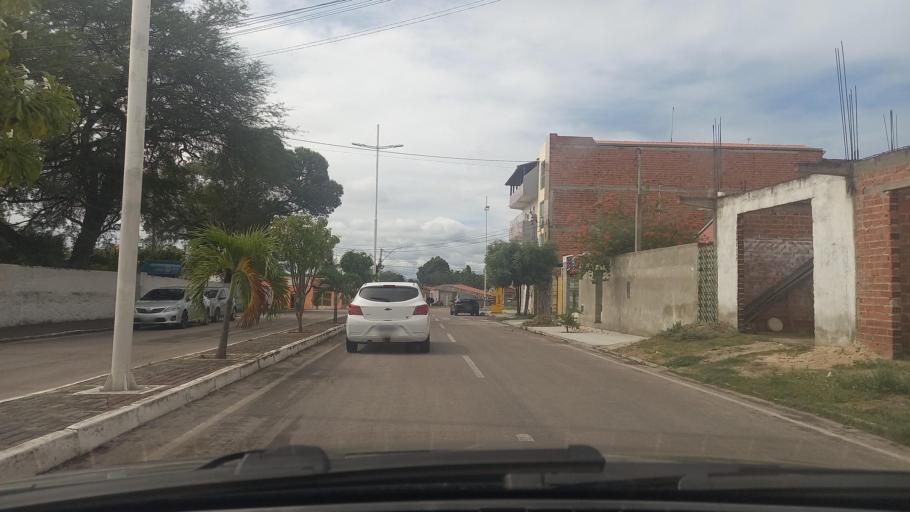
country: BR
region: Bahia
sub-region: Paulo Afonso
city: Paulo Afonso
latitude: -9.4384
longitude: -38.2124
